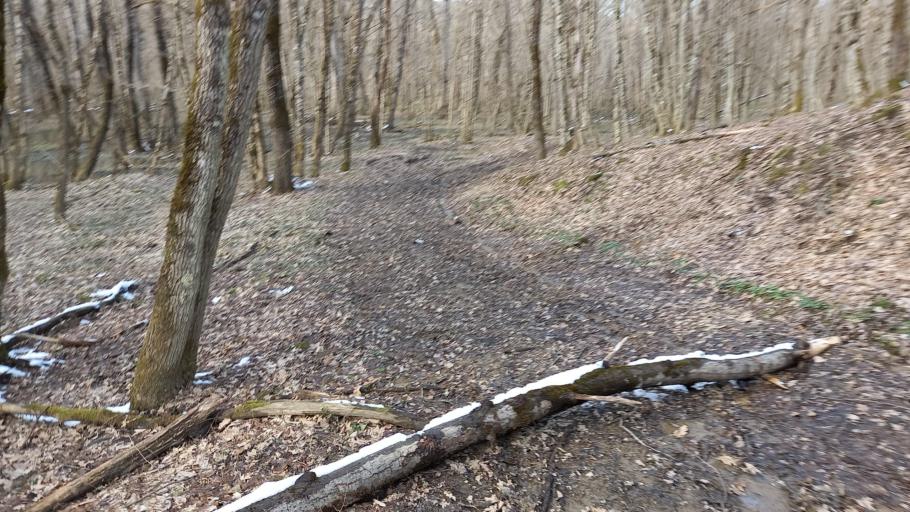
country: RU
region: Krasnodarskiy
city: Smolenskaya
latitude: 44.5961
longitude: 38.8470
